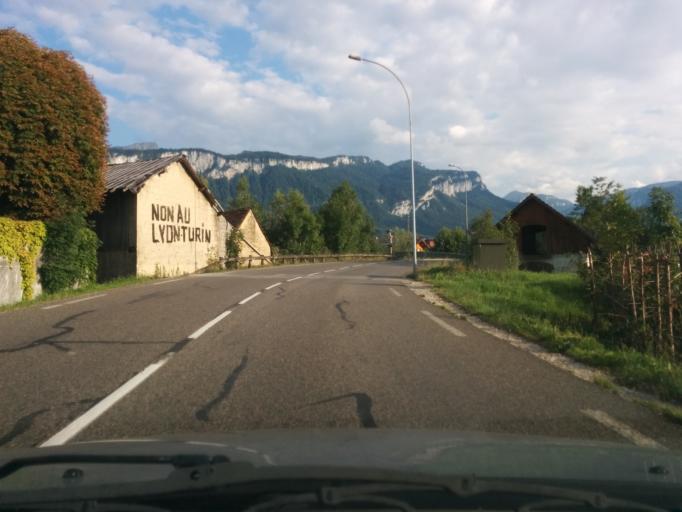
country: FR
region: Rhone-Alpes
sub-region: Departement de la Savoie
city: Les Echelles
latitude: 45.4357
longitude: 5.7523
